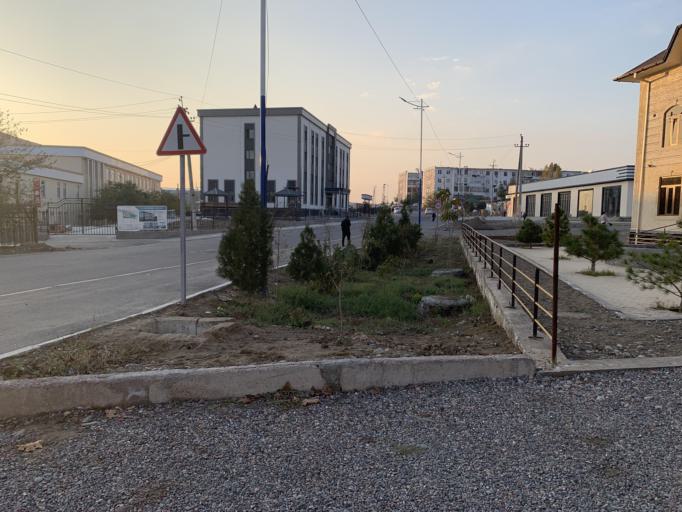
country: UZ
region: Namangan
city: Namangan Shahri
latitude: 41.0021
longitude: 71.5992
